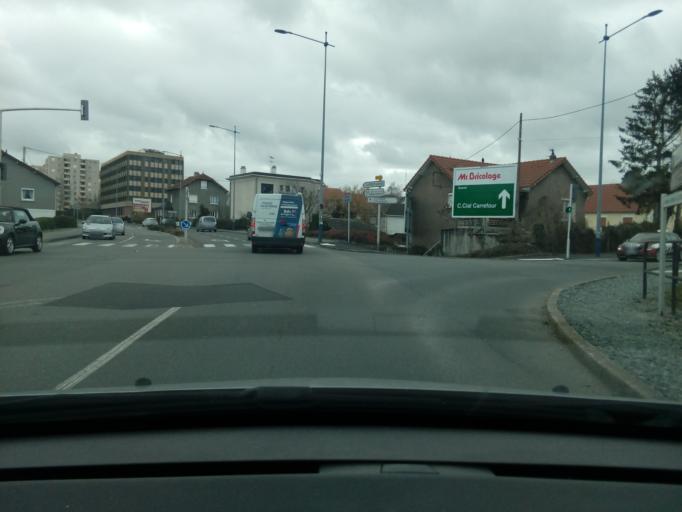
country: FR
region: Limousin
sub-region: Departement de la Creuse
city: Gueret
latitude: 46.1794
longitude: 1.8724
